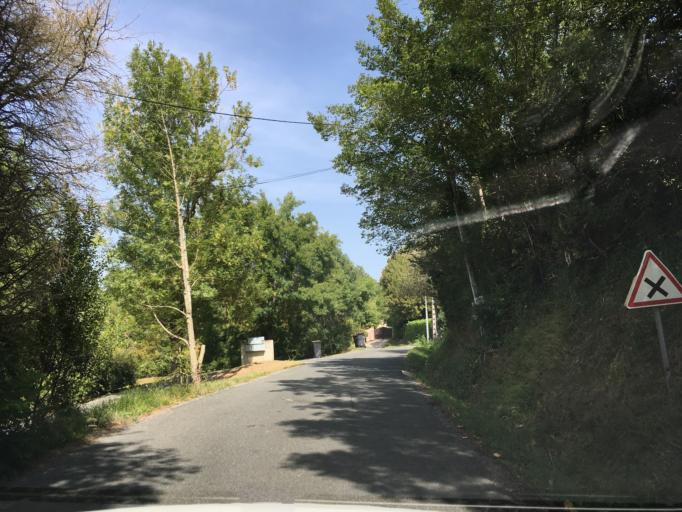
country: FR
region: Midi-Pyrenees
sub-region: Departement du Tarn
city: Castres
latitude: 43.6285
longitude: 2.2339
